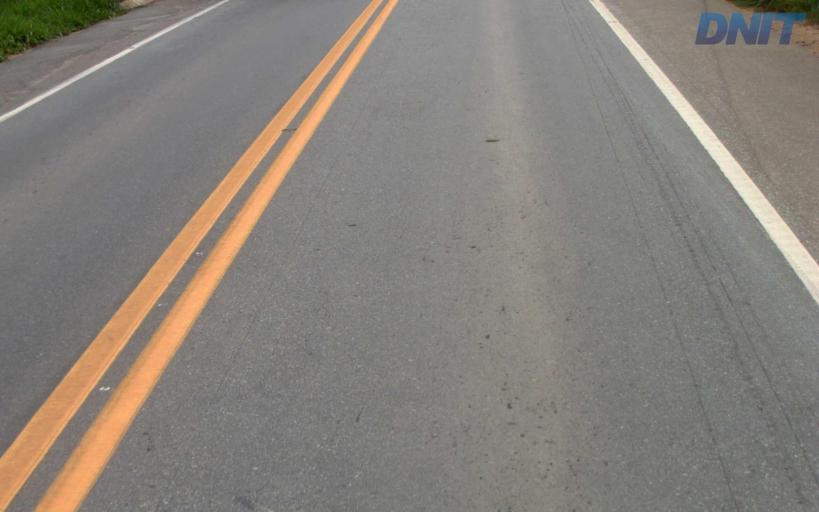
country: BR
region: Minas Gerais
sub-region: Governador Valadares
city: Governador Valadares
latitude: -18.9524
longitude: -42.0722
